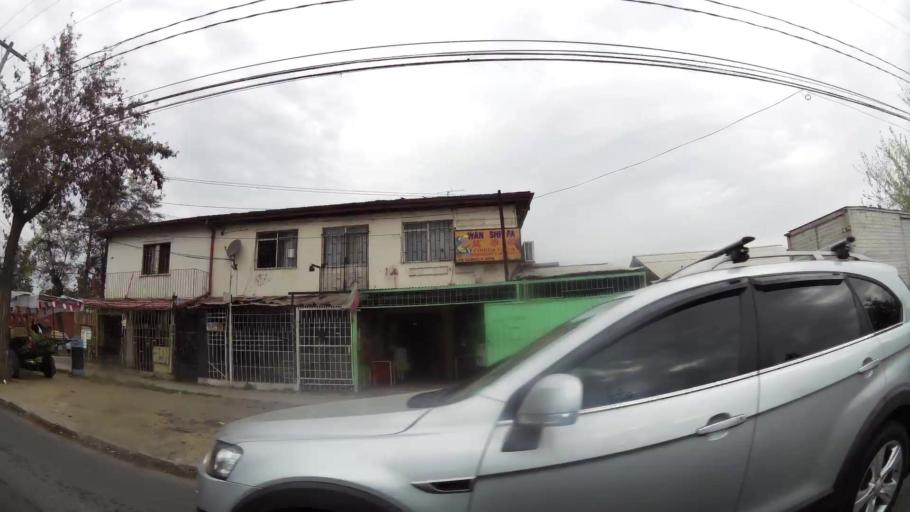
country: CL
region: Santiago Metropolitan
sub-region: Provincia de Santiago
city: Villa Presidente Frei, Nunoa, Santiago, Chile
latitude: -33.4799
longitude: -70.5898
